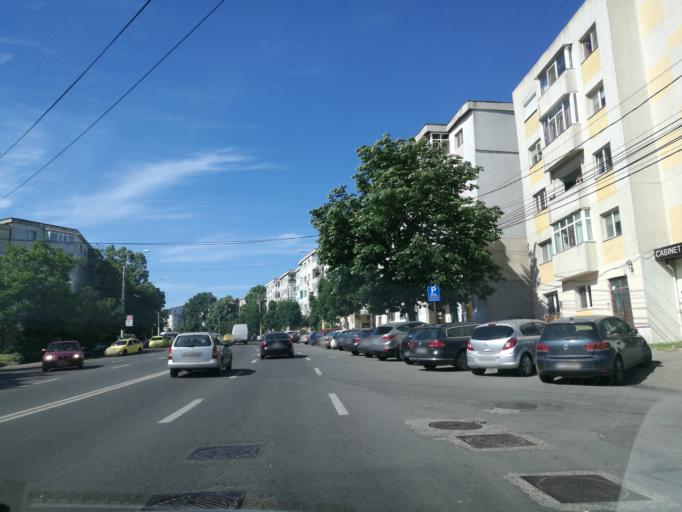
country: RO
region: Constanta
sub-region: Municipiul Constanta
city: Constanta
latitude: 44.1996
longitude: 28.6255
